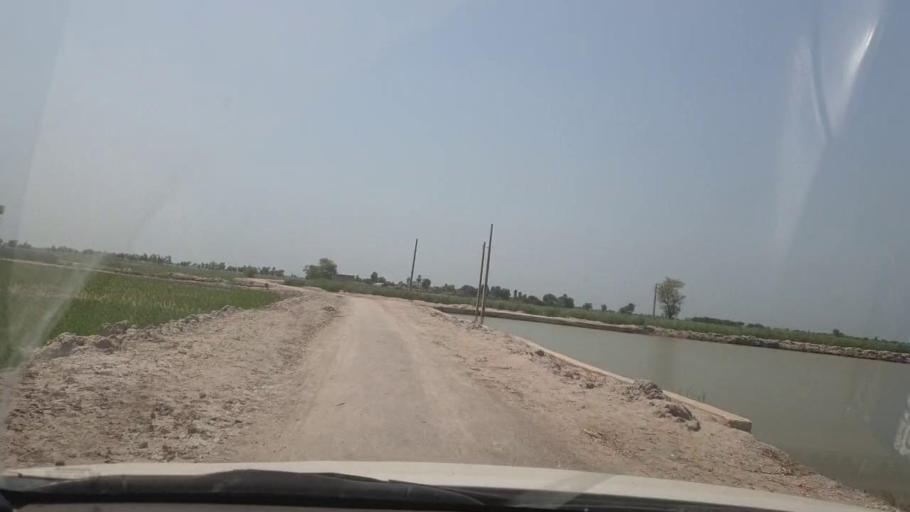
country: PK
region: Sindh
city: Lakhi
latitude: 27.8769
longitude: 68.7352
